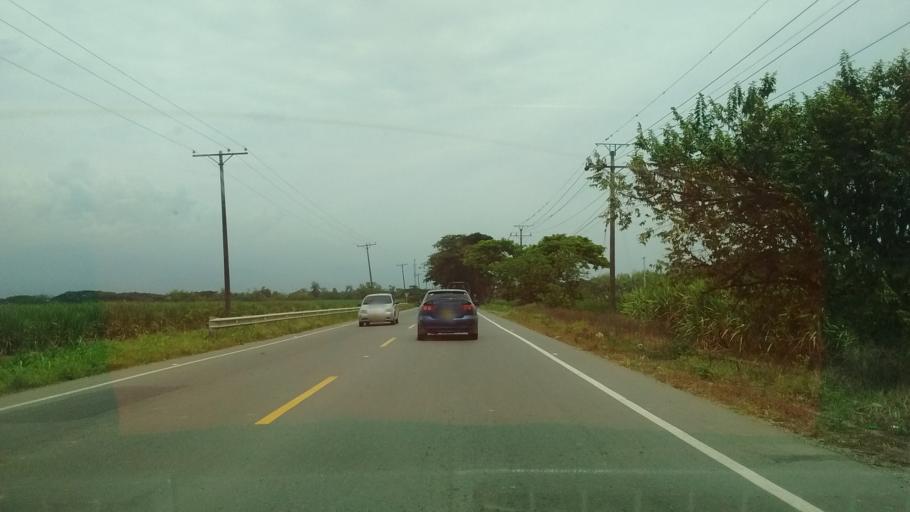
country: CO
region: Valle del Cauca
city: Jamundi
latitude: 3.2952
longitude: -76.4709
